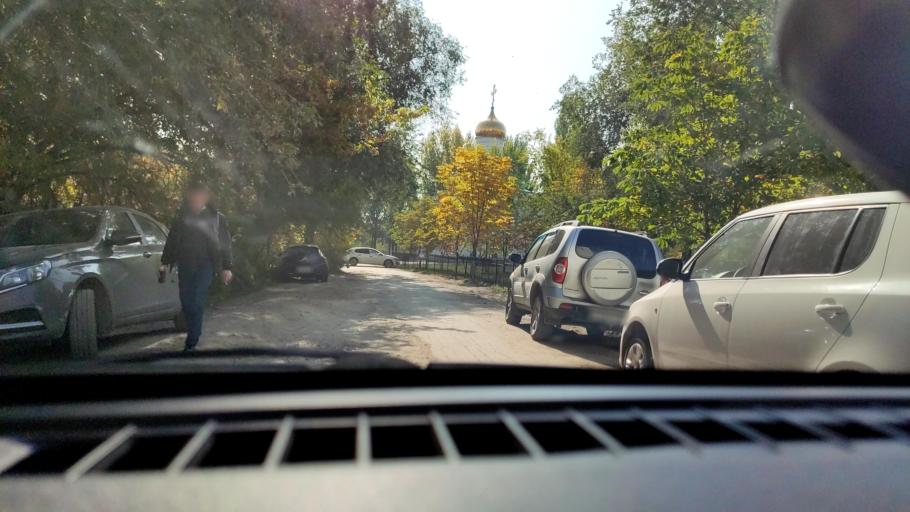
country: RU
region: Samara
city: Samara
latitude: 53.1936
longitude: 50.2060
